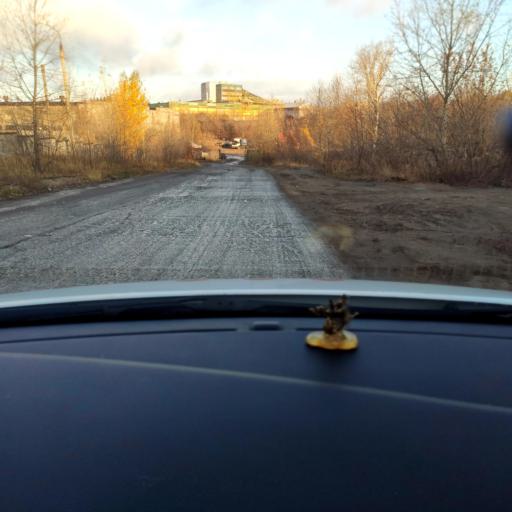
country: RU
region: Tatarstan
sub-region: Gorod Kazan'
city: Kazan
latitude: 55.7770
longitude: 49.1843
